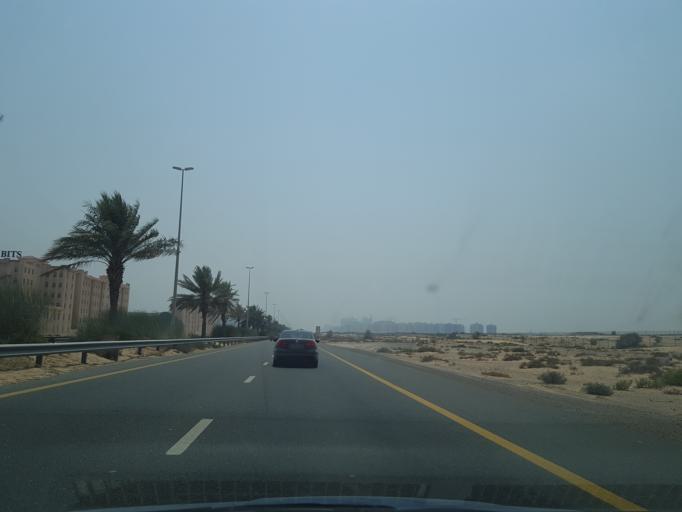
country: AE
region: Ash Shariqah
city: Sharjah
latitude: 25.1345
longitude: 55.4208
